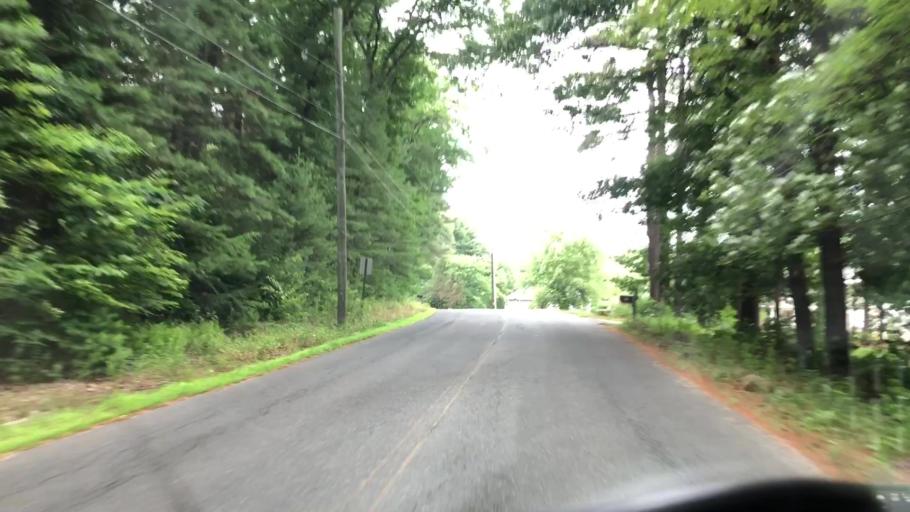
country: US
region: Massachusetts
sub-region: Hampshire County
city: Southampton
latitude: 42.2173
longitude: -72.6812
